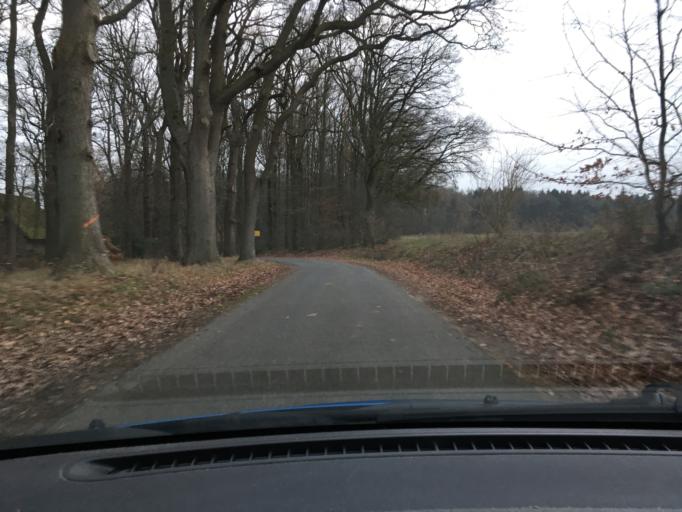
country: DE
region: Lower Saxony
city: Walsrode
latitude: 52.8355
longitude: 9.5691
